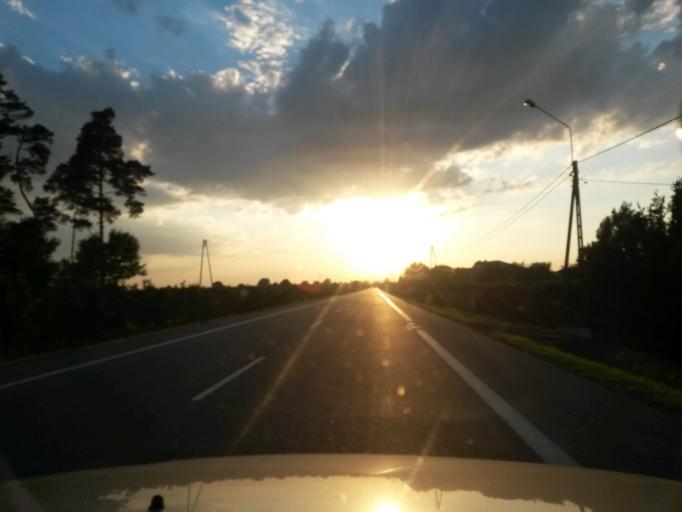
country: PL
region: Lodz Voivodeship
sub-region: Powiat wielunski
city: Czarnozyly
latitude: 51.2531
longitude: 18.5042
